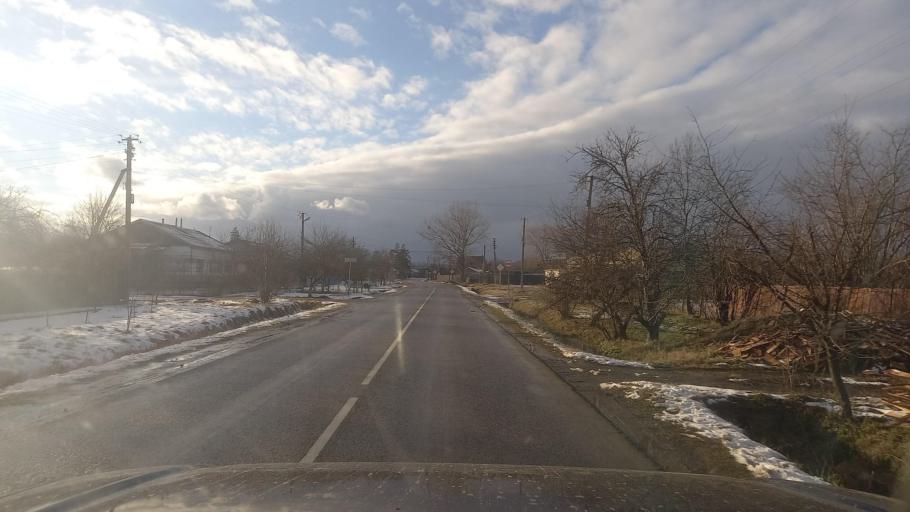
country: RU
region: Krasnodarskiy
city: Smolenskaya
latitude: 44.7765
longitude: 38.8416
